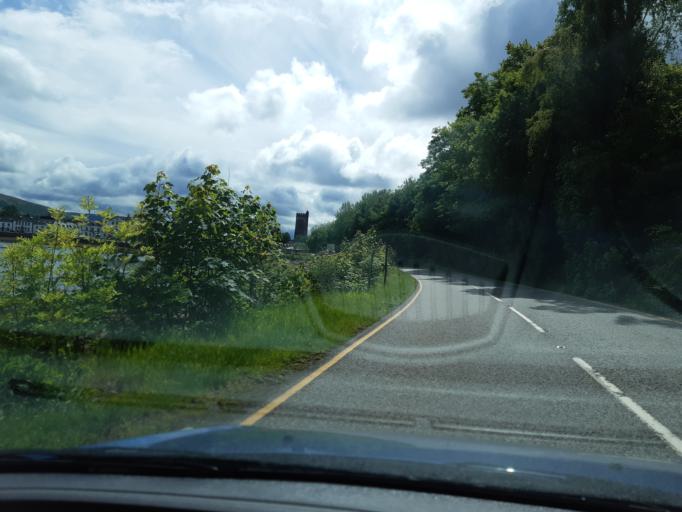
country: GB
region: Scotland
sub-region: Argyll and Bute
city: Garelochhead
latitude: 56.2346
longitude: -5.0724
